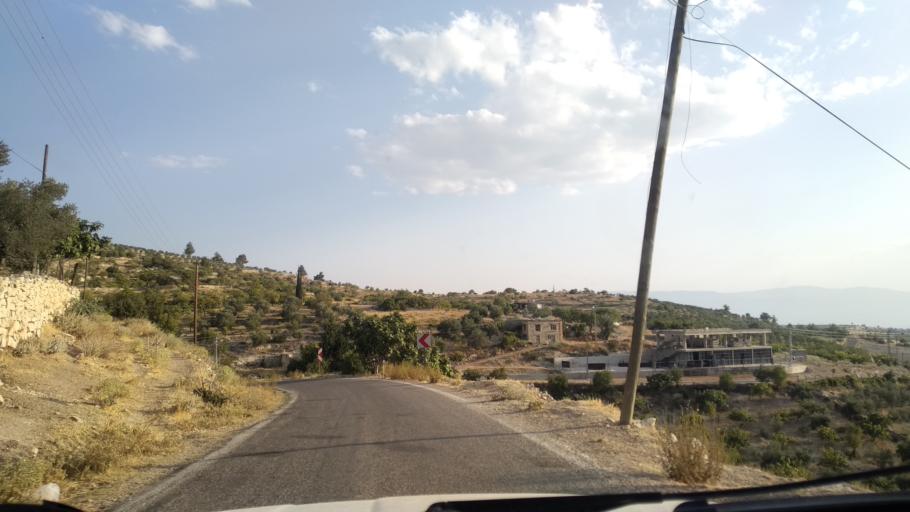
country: TR
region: Mersin
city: Sarikavak
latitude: 36.5779
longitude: 33.6436
